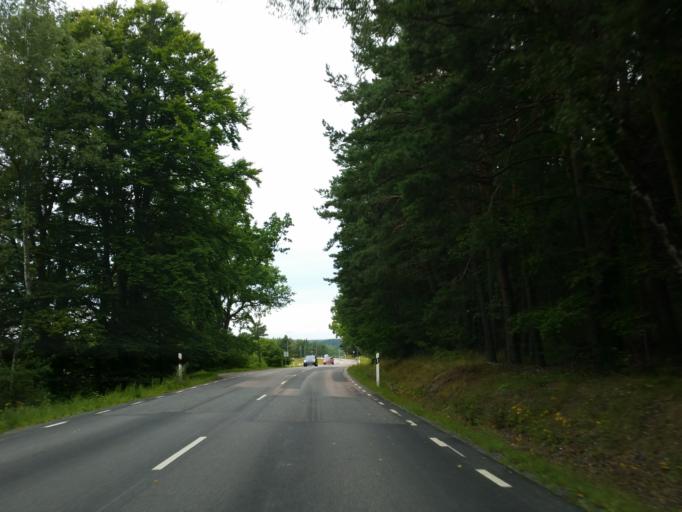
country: SE
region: Stockholm
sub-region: Nykvarns Kommun
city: Nykvarn
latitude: 59.1893
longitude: 17.4731
